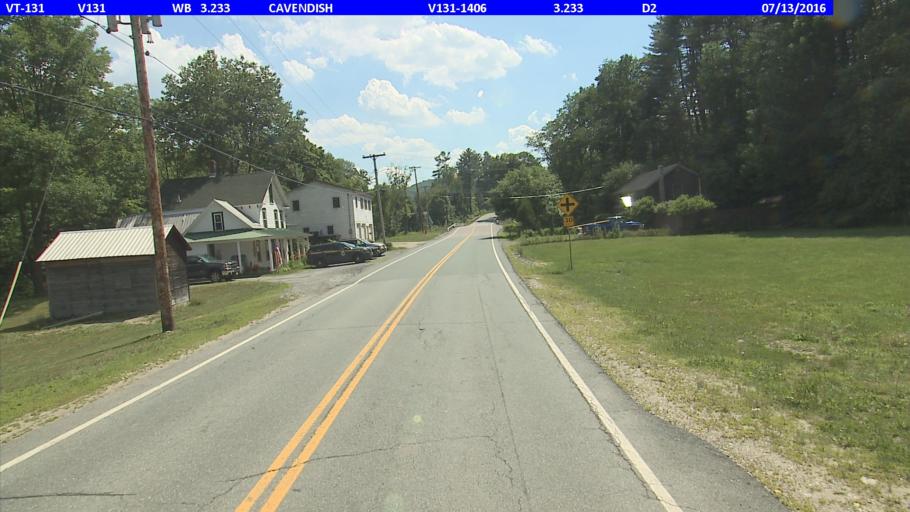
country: US
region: Vermont
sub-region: Windsor County
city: Chester
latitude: 43.3935
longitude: -72.5935
